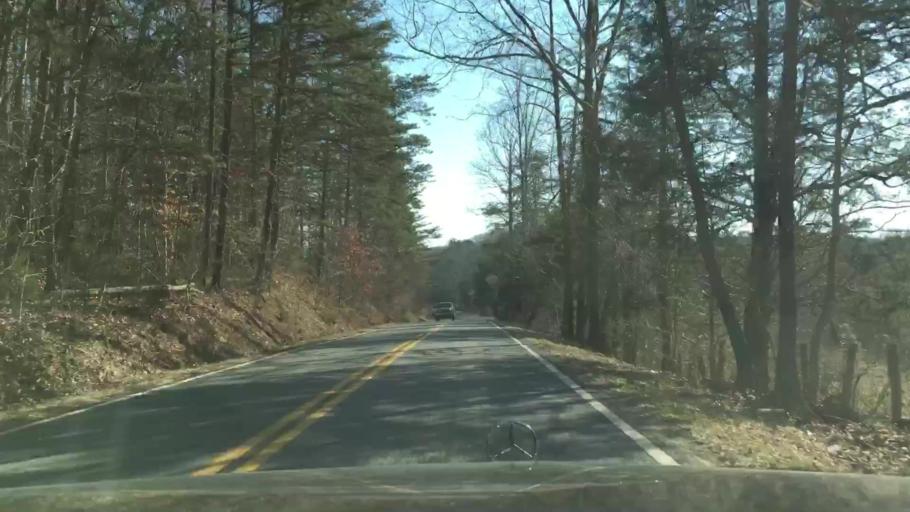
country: US
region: Virginia
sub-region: Campbell County
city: Altavista
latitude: 37.1539
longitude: -79.3603
